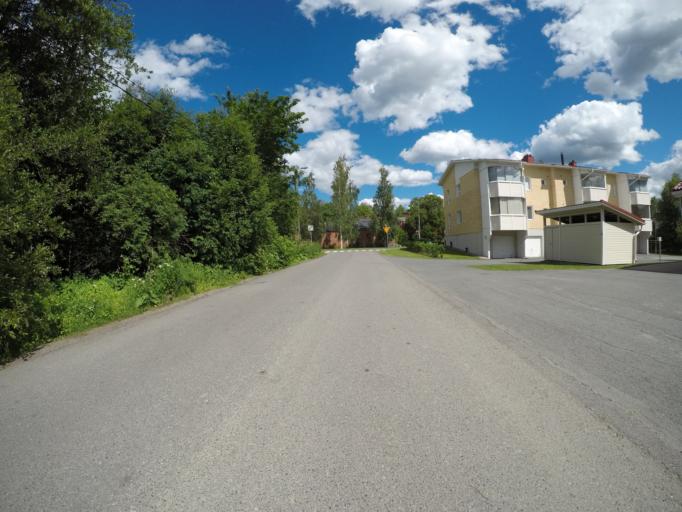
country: FI
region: Haeme
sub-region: Haemeenlinna
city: Haemeenlinna
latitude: 61.0036
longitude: 24.4544
